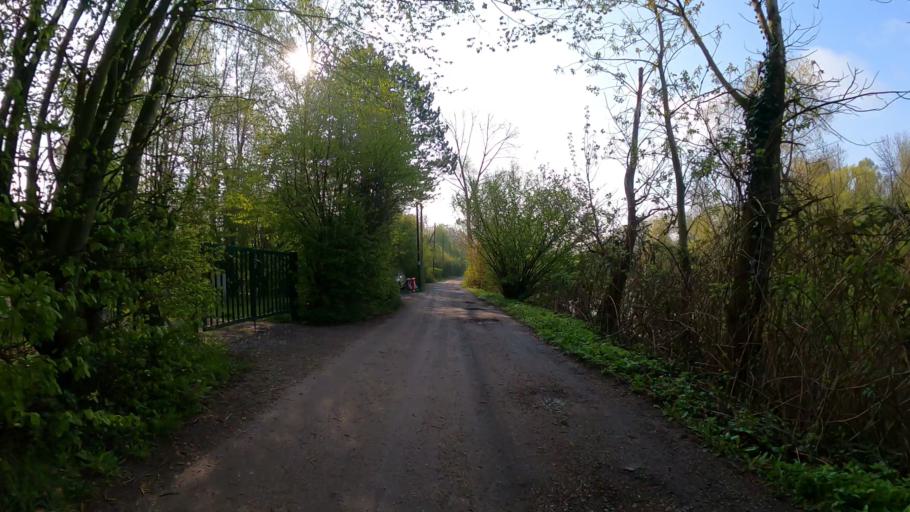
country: DE
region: Hamburg
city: Kleiner Grasbrook
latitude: 53.5061
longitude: 10.0167
